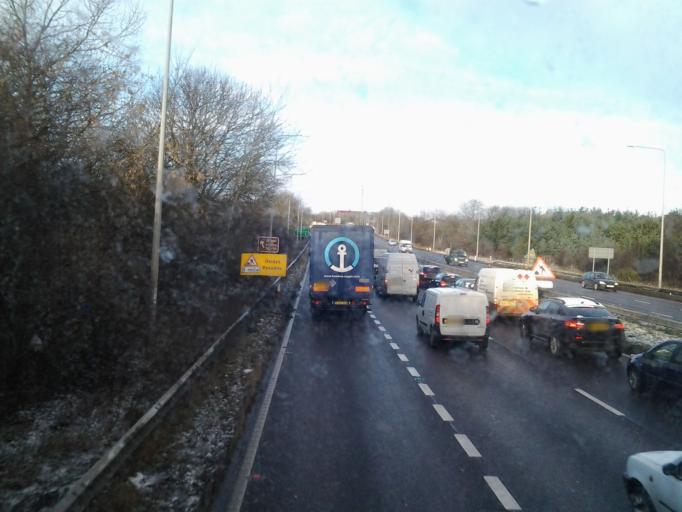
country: GB
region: England
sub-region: Gateshead
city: Lamesley
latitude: 54.9080
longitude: -1.5730
